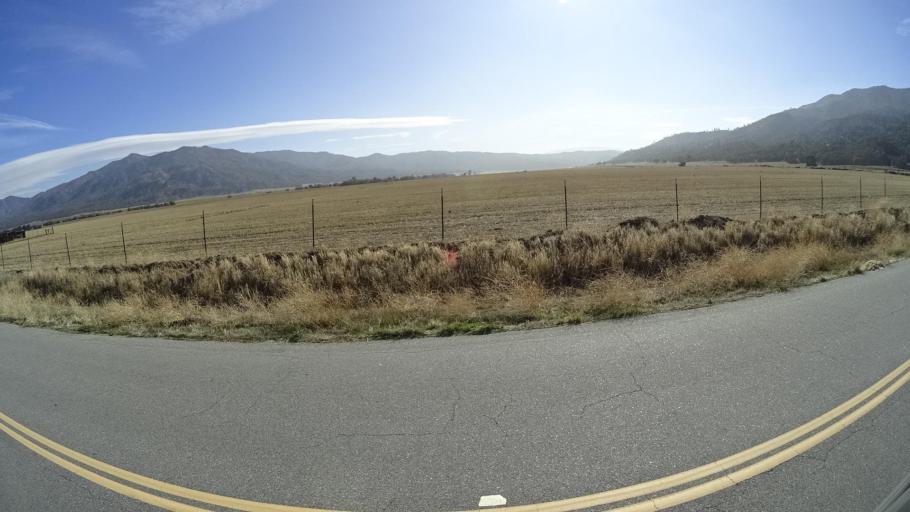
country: US
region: California
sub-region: Kern County
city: Bodfish
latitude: 35.4188
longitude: -118.5417
